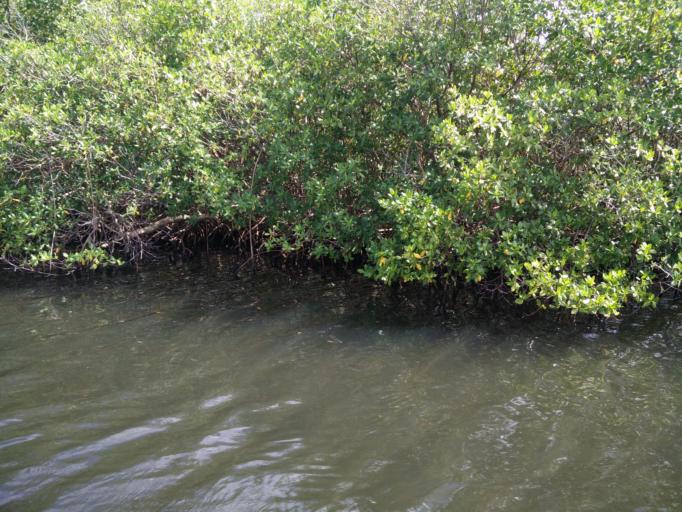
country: GP
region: Guadeloupe
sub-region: Guadeloupe
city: Petit-Canal
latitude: 16.3551
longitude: -61.4985
